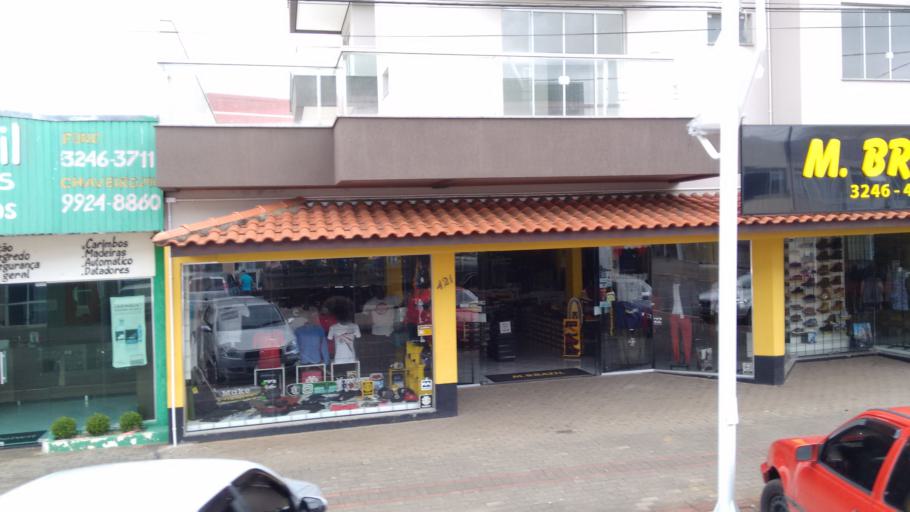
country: BR
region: Santa Catarina
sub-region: Videira
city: Videira
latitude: -27.0238
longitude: -50.9257
